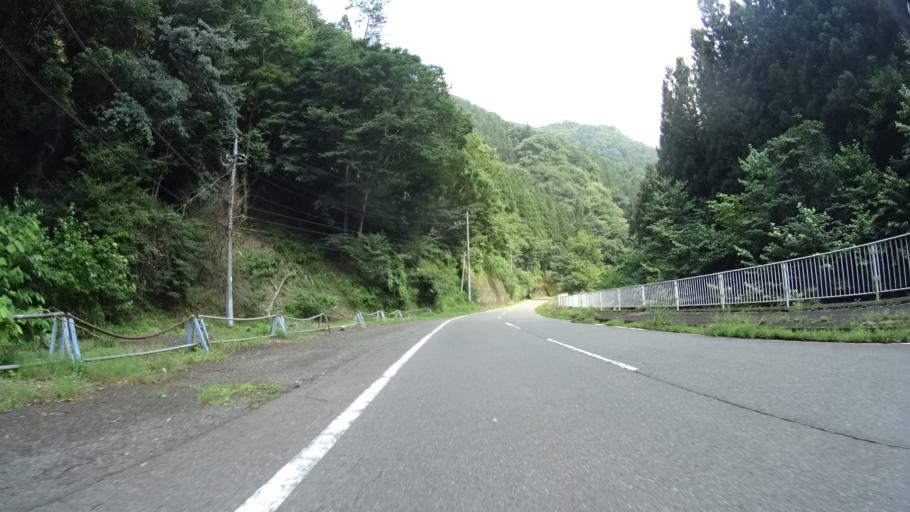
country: JP
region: Gunma
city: Tomioka
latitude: 36.0817
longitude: 138.8240
